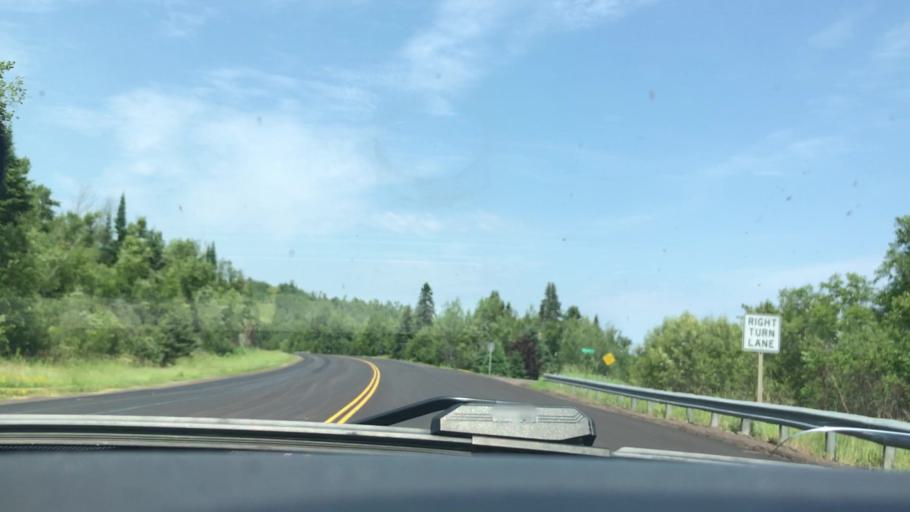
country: US
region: Minnesota
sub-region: Lake County
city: Silver Bay
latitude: 47.3619
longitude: -91.1745
